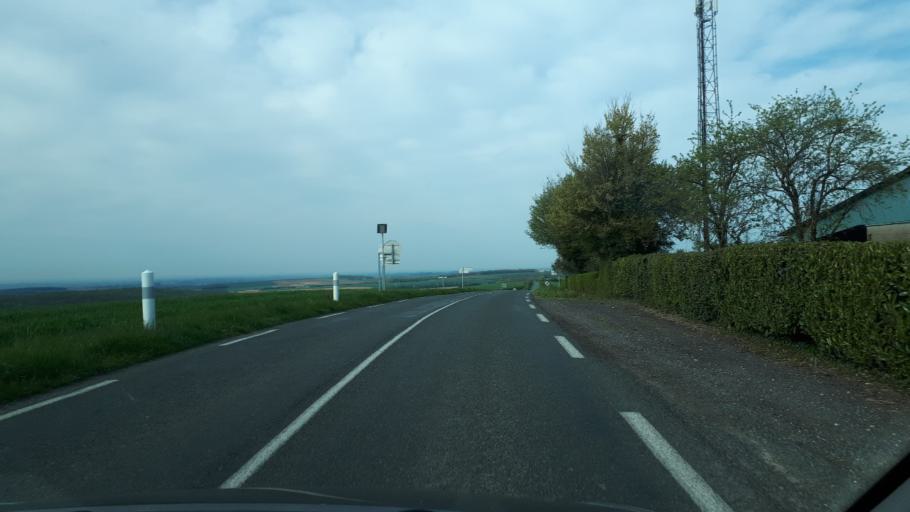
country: FR
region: Centre
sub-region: Departement du Cher
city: Rians
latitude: 47.2454
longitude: 2.6685
